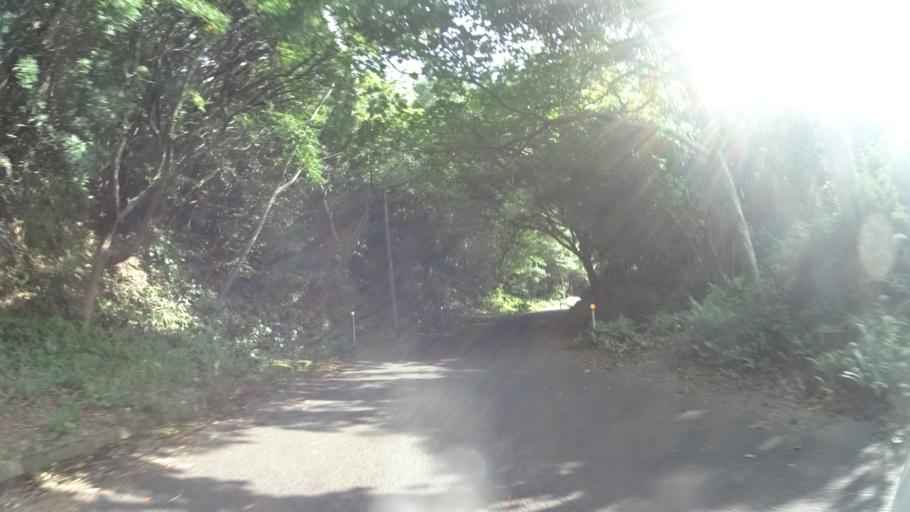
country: JP
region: Kagoshima
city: Nishinoomote
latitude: 30.3883
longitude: 130.3867
